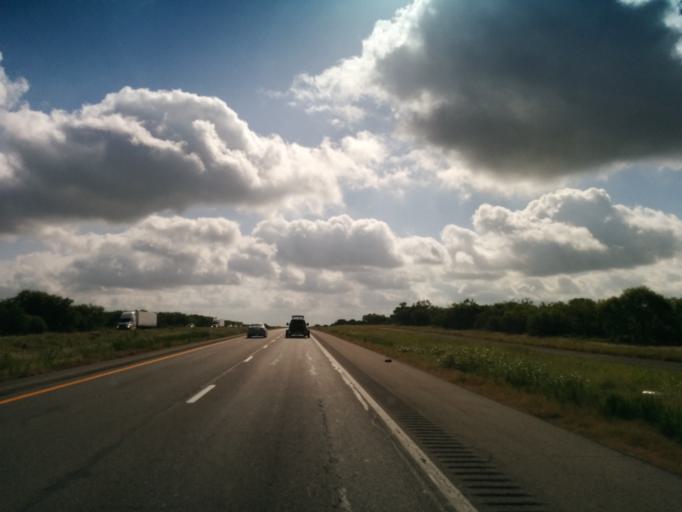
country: US
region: Texas
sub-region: Caldwell County
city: Luling
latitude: 29.6395
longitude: -97.7173
